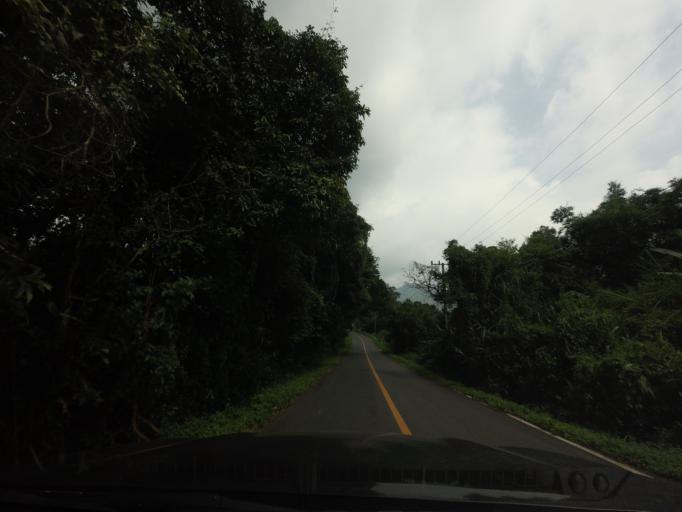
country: TH
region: Nan
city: Bo Kluea
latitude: 19.1881
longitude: 101.0399
